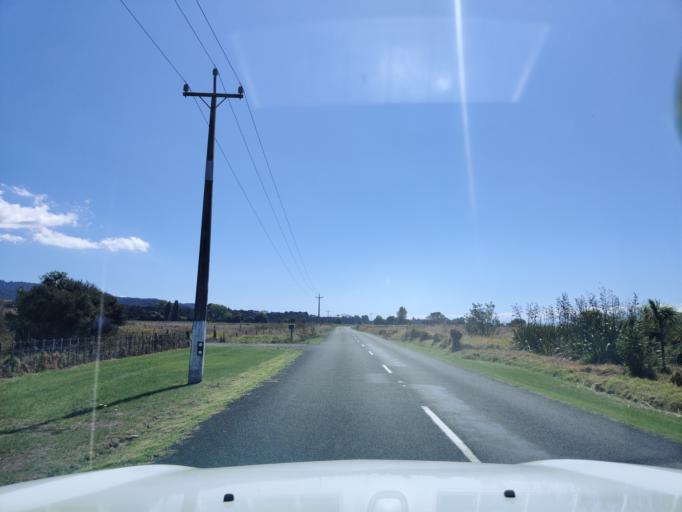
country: NZ
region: Waikato
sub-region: Thames-Coromandel District
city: Thames
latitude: -37.0717
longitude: 175.2958
